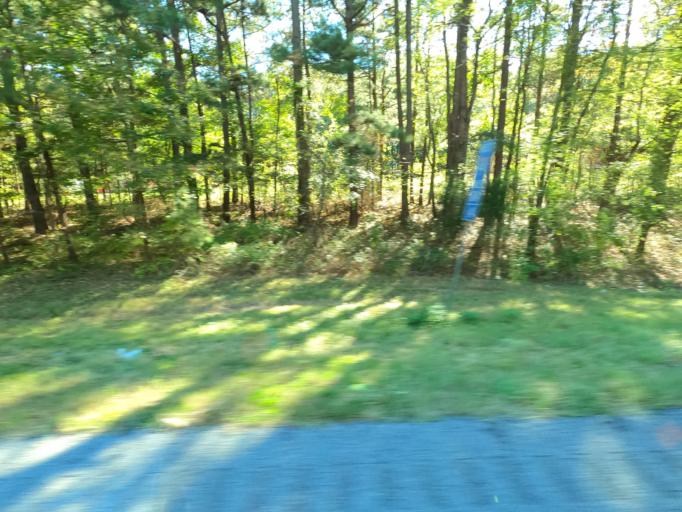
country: US
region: Tennessee
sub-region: Cheatham County
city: Kingston Springs
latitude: 36.0491
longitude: -87.1433
